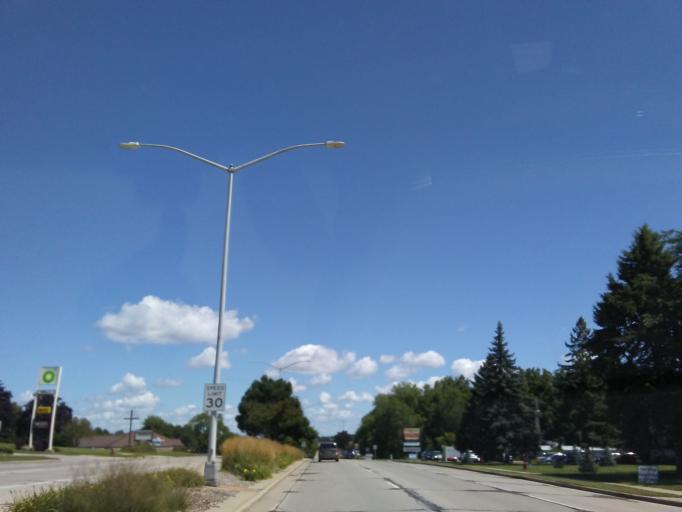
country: US
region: Wisconsin
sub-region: Dane County
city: Madison
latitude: 43.0274
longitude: -89.4120
